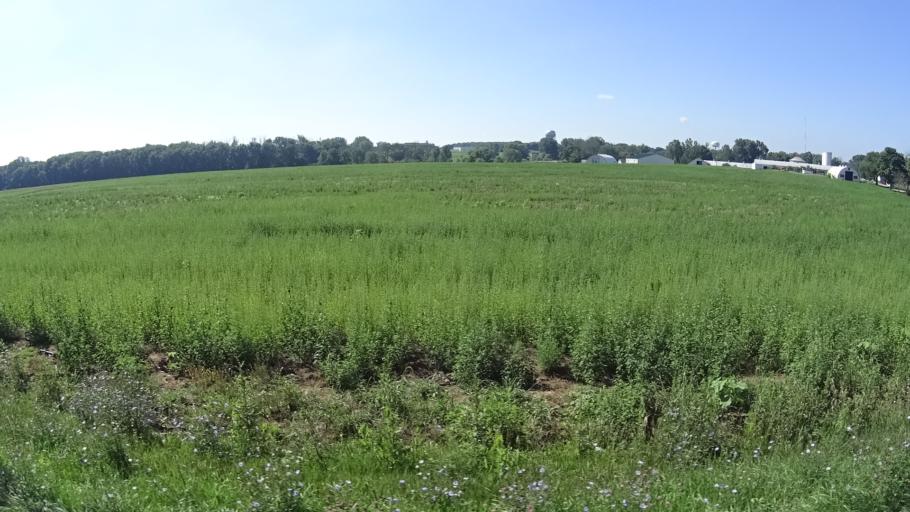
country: US
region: Indiana
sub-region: Madison County
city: Pendleton
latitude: 39.9890
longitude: -85.7698
